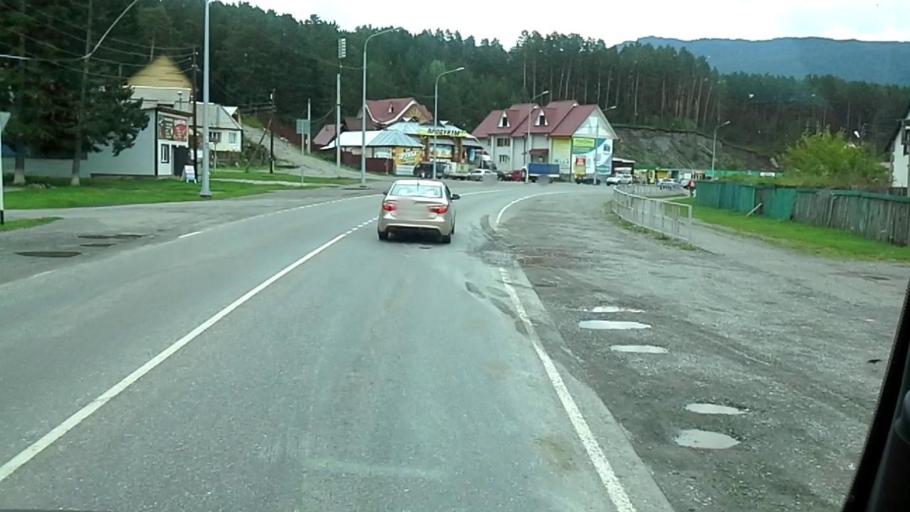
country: RU
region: Altay
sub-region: Mayminskiy Rayon
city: Manzherok
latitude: 51.8337
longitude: 85.7792
